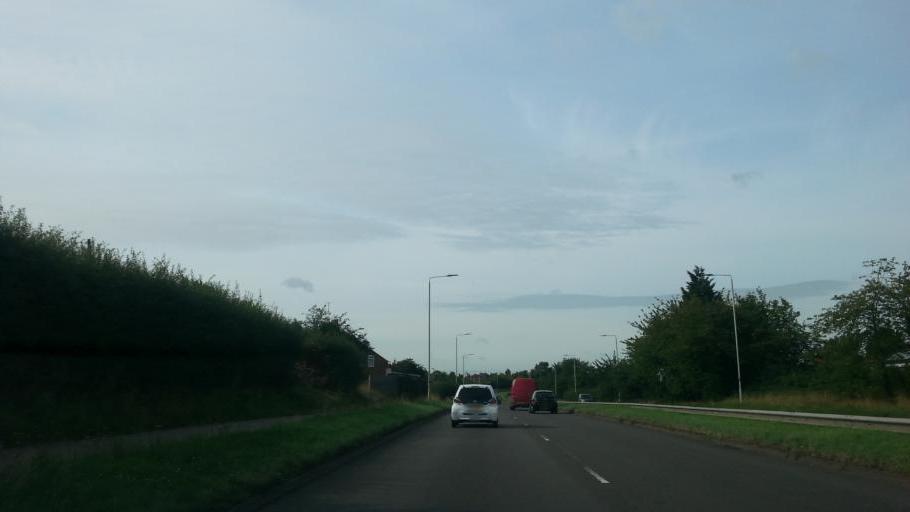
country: GB
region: England
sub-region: Leicestershire
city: Syston
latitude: 52.6779
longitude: -1.0960
